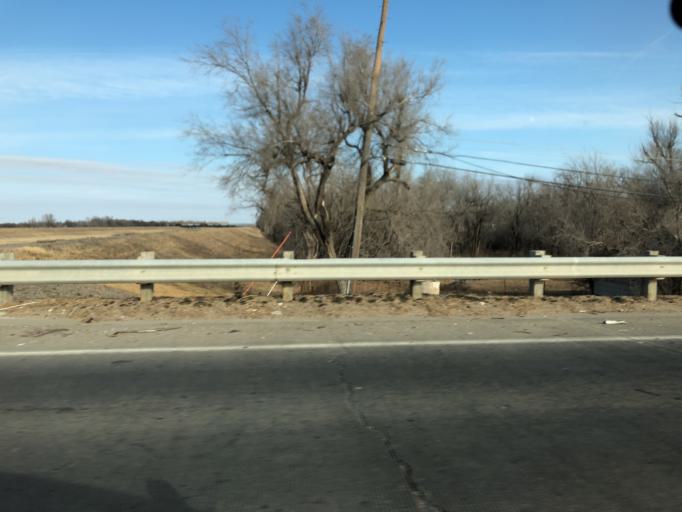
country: US
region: Kansas
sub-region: Reno County
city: Hutchinson
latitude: 38.0572
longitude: -97.9662
